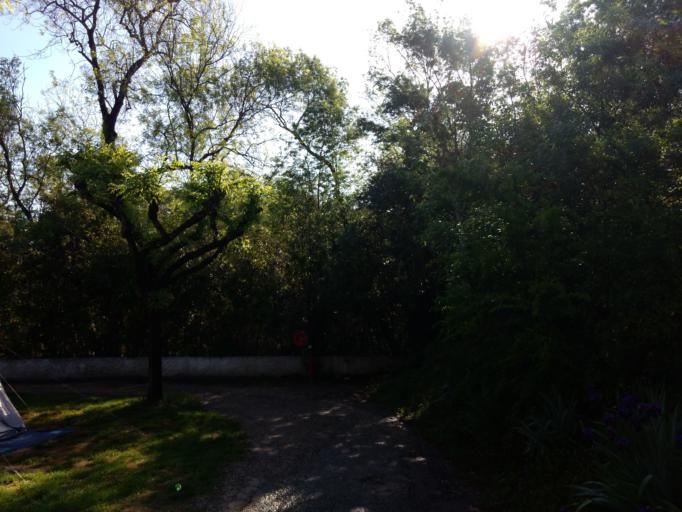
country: FR
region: Provence-Alpes-Cote d'Azur
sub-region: Departement des Alpes-Maritimes
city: Biot
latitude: 43.6198
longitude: 7.1272
